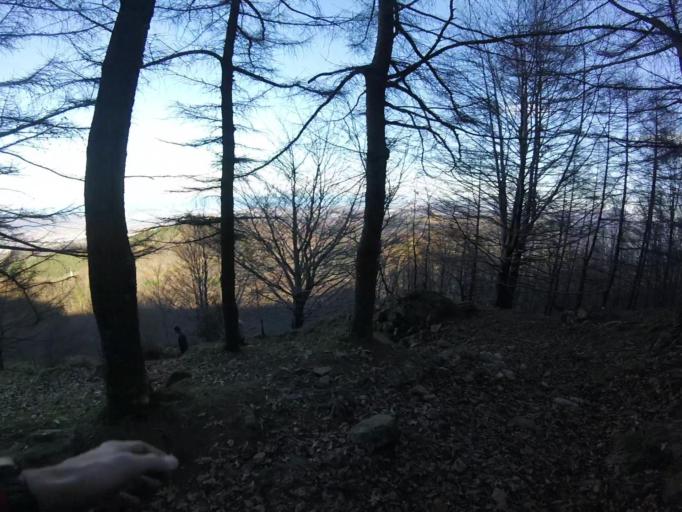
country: ES
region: Basque Country
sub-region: Provincia de Guipuzcoa
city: Irun
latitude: 43.2893
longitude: -1.7833
